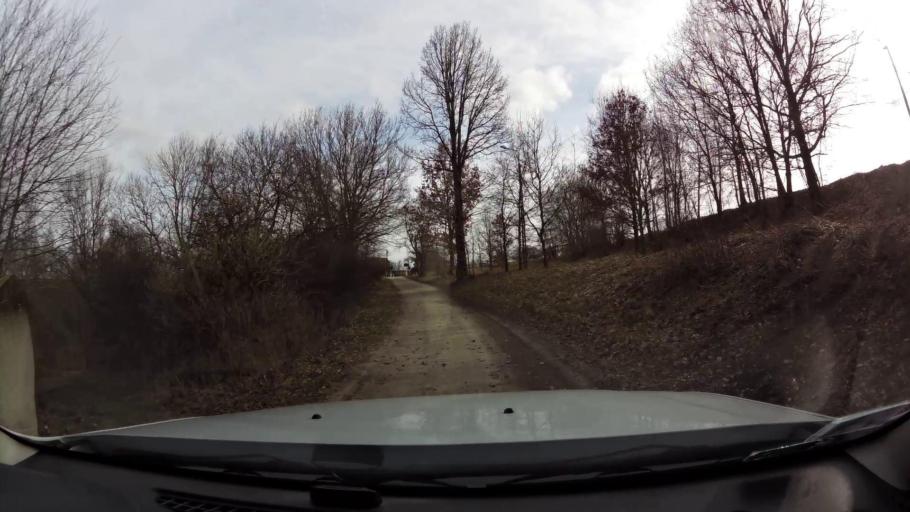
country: PL
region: West Pomeranian Voivodeship
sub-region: Powiat drawski
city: Drawsko Pomorskie
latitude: 53.5145
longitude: 15.7496
